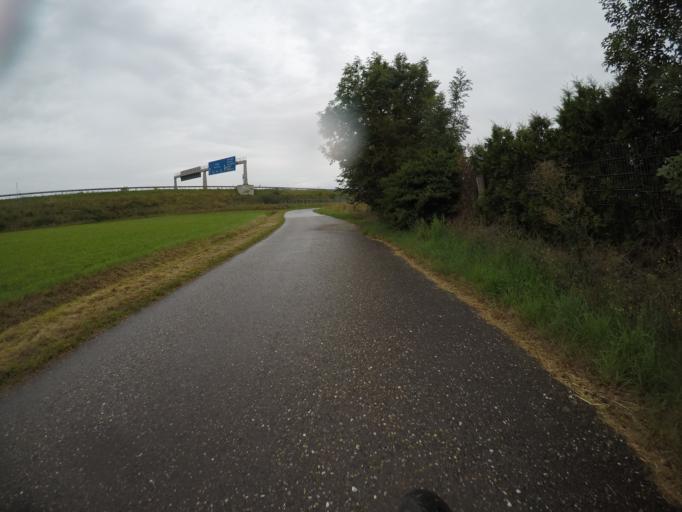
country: DE
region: Baden-Wuerttemberg
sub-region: Regierungsbezirk Stuttgart
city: Ehningen
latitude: 48.6450
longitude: 8.9356
